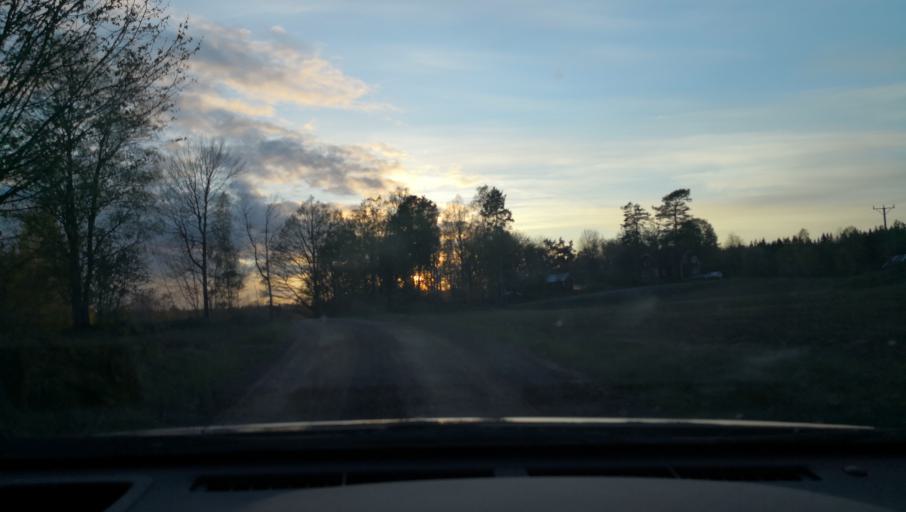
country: SE
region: OErebro
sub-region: Askersunds Kommun
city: Askersund
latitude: 58.9732
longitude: 14.9475
